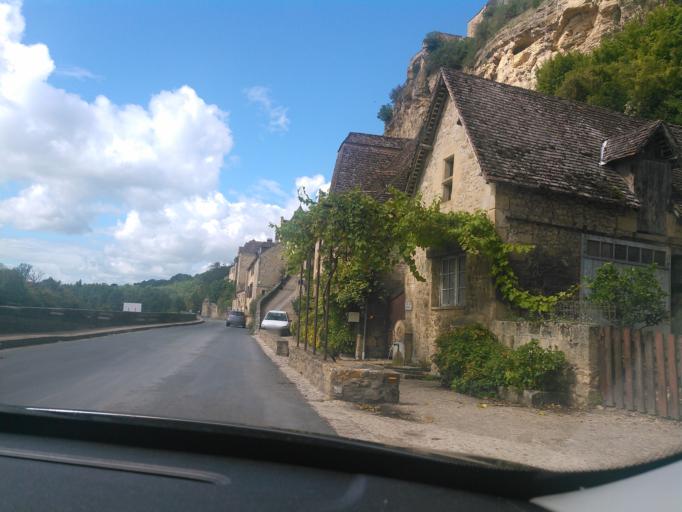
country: FR
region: Aquitaine
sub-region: Departement de la Dordogne
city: Cenac-et-Saint-Julien
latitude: 44.8392
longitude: 1.1467
